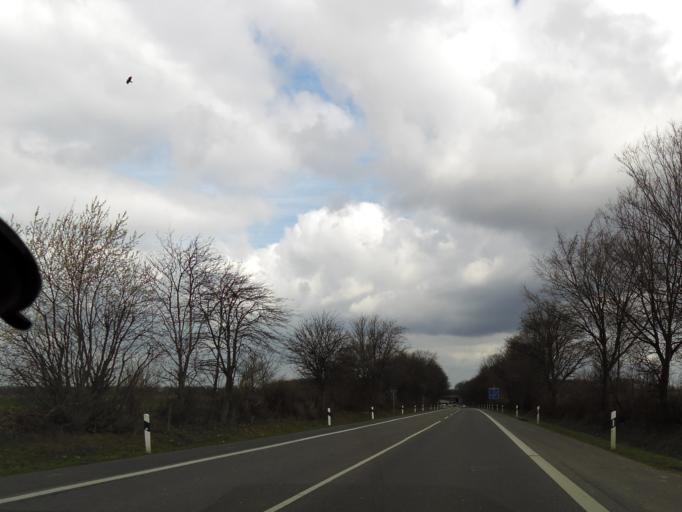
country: DE
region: North Rhine-Westphalia
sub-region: Regierungsbezirk Koln
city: Rheinbach
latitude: 50.6164
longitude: 6.9750
